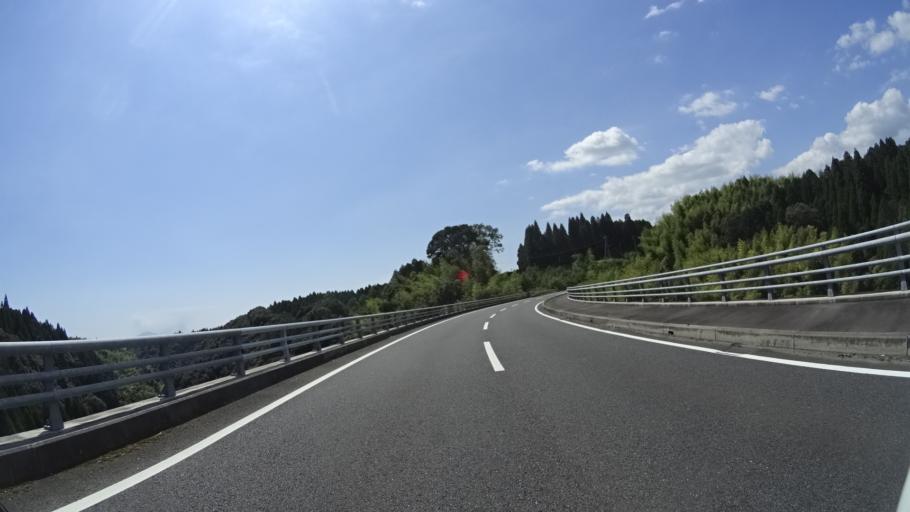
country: JP
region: Kagoshima
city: Kajiki
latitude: 31.8136
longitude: 130.6985
